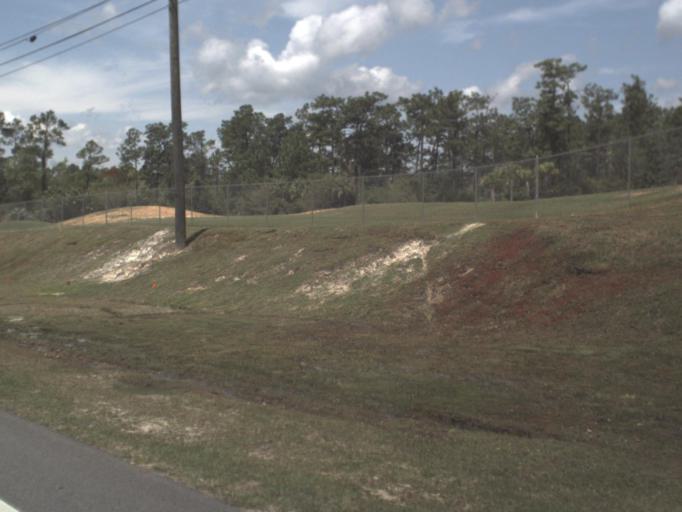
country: US
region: Florida
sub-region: Escambia County
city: Gonzalez
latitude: 30.5348
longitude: -87.3403
